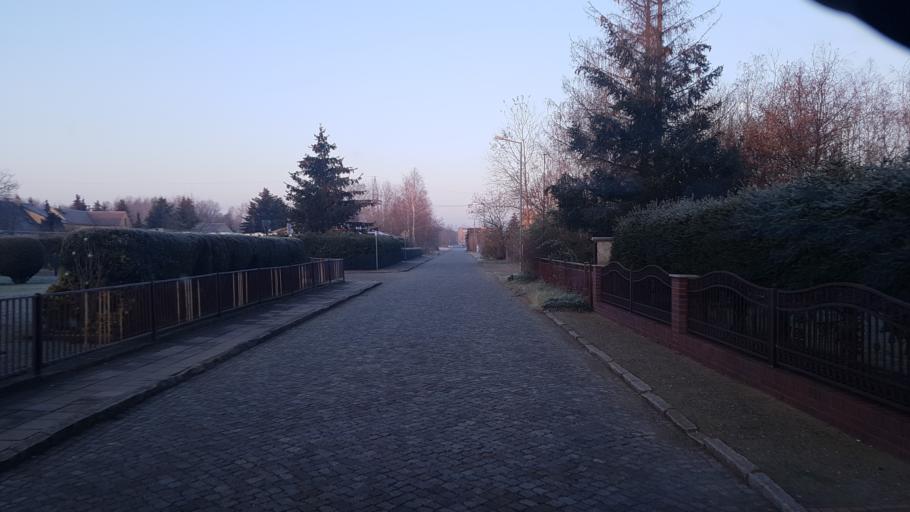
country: DE
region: Brandenburg
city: Lauchhammer
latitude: 51.4836
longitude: 13.7271
